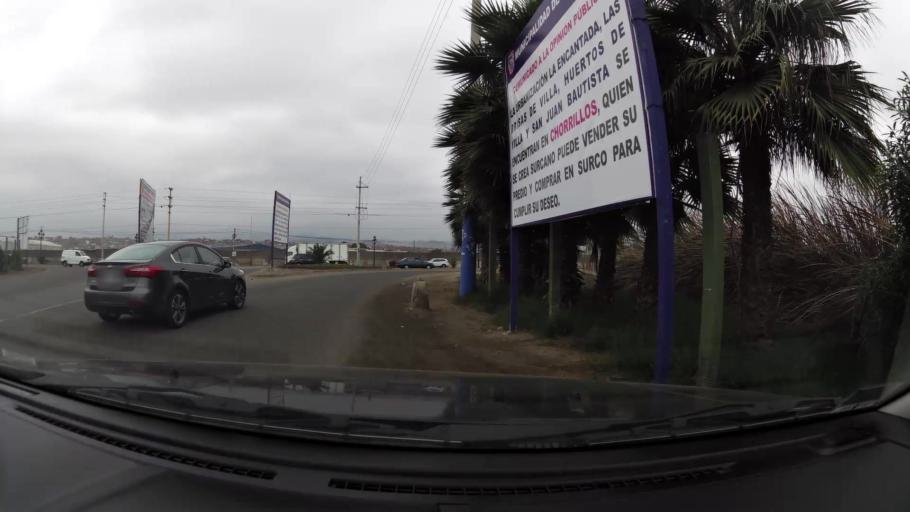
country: PE
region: Lima
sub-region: Lima
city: Surco
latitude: -12.2097
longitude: -76.9879
